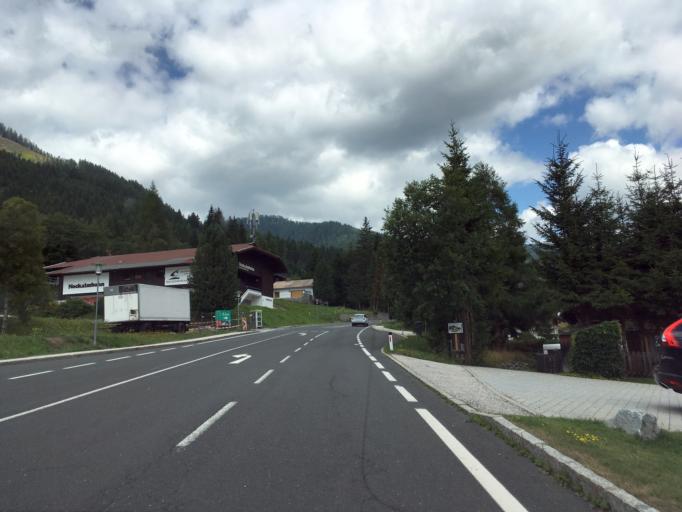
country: AT
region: Carinthia
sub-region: Politischer Bezirk Spittal an der Drau
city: Kleinkirchheim
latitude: 46.8303
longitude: 13.7643
